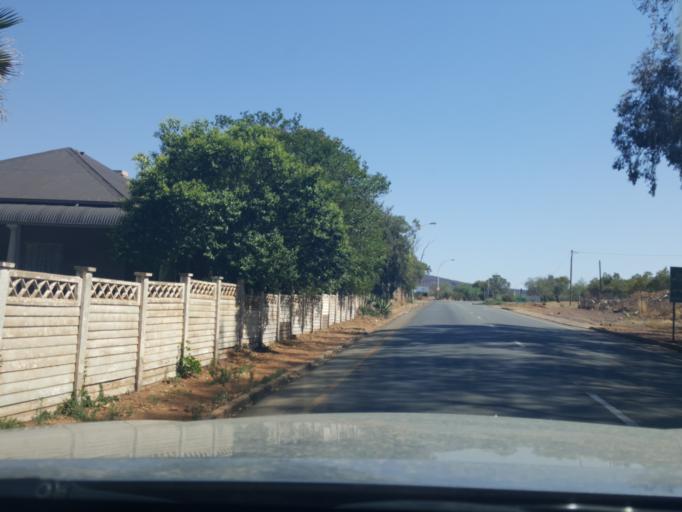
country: ZA
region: North-West
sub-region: Ngaka Modiri Molema District Municipality
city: Zeerust
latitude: -25.5403
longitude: 26.0777
